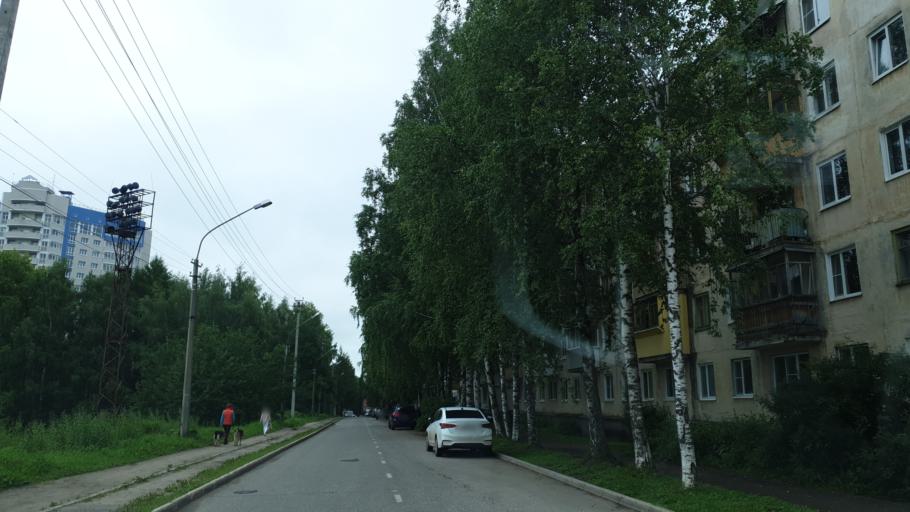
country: RU
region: Komi Republic
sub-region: Syktyvdinskiy Rayon
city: Syktyvkar
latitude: 61.6624
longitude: 50.8244
